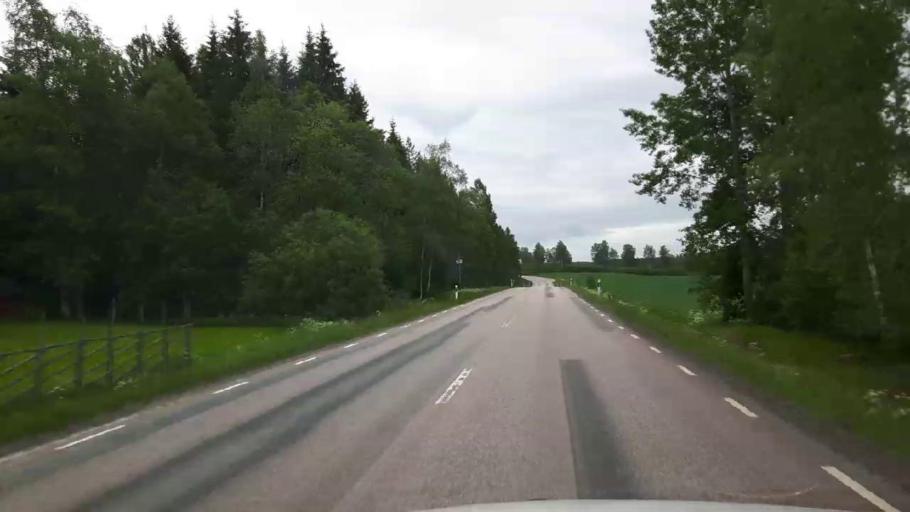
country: SE
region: Vaestmanland
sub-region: Kopings Kommun
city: Kolsva
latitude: 59.6215
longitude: 15.8204
